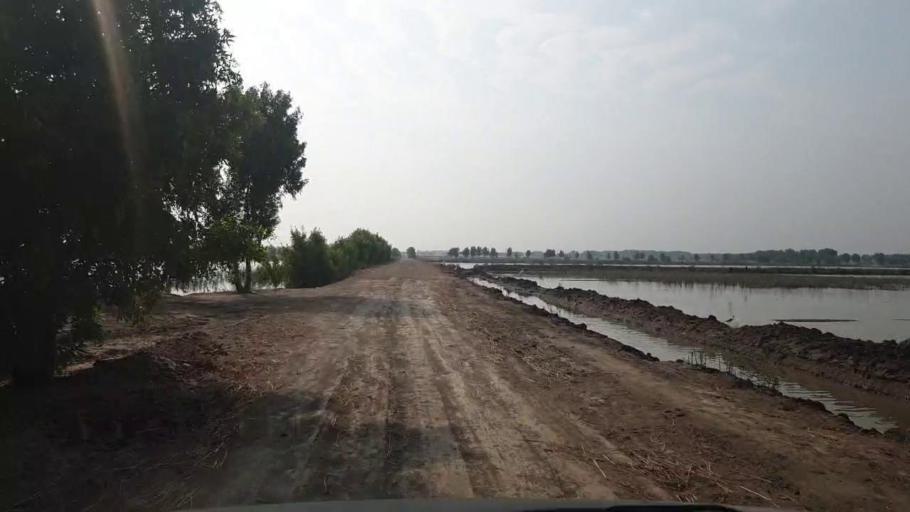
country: PK
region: Sindh
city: Tando Muhammad Khan
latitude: 25.0994
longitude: 68.5070
